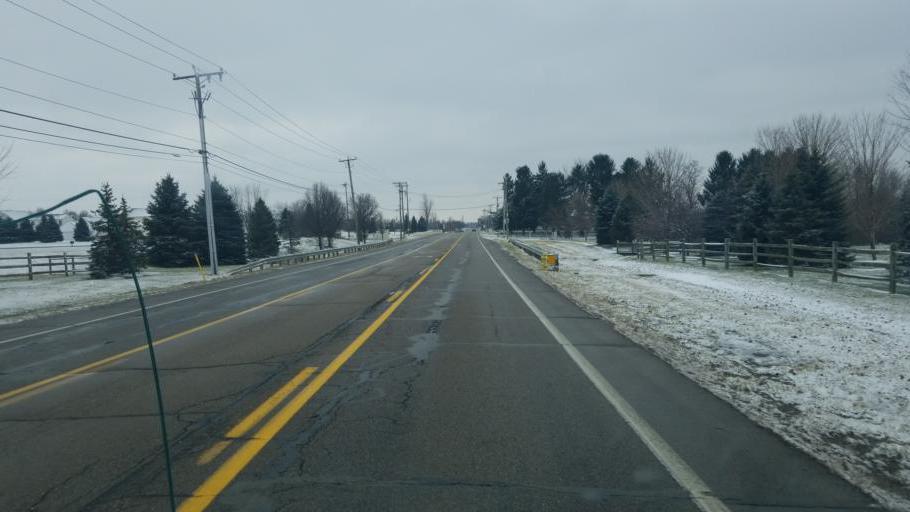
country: US
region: Ohio
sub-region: Franklin County
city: Reynoldsburg
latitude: 40.0159
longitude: -82.7900
